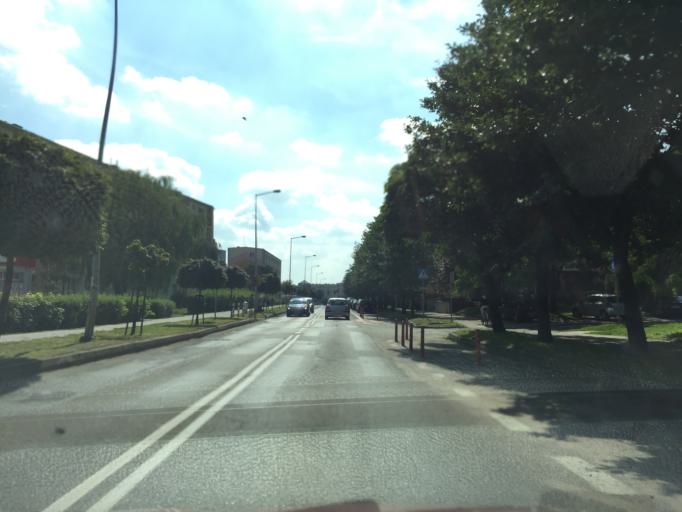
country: PL
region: Greater Poland Voivodeship
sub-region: Kalisz
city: Kalisz
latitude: 51.7490
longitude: 18.0693
